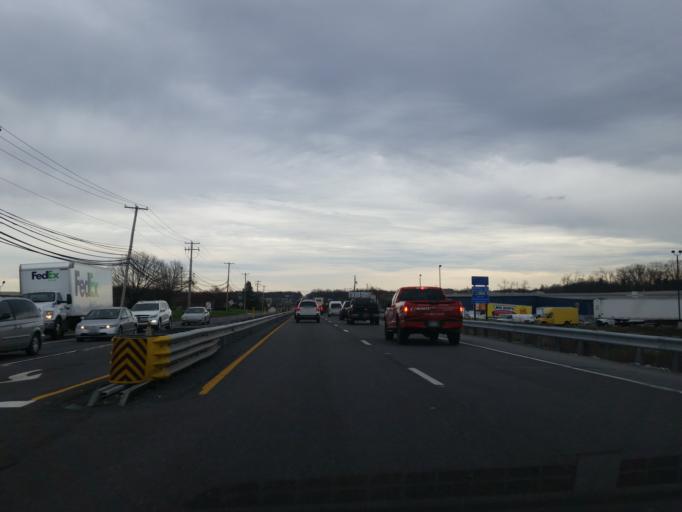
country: US
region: Pennsylvania
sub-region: Dauphin County
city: Linglestown
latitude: 40.3245
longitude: -76.7814
